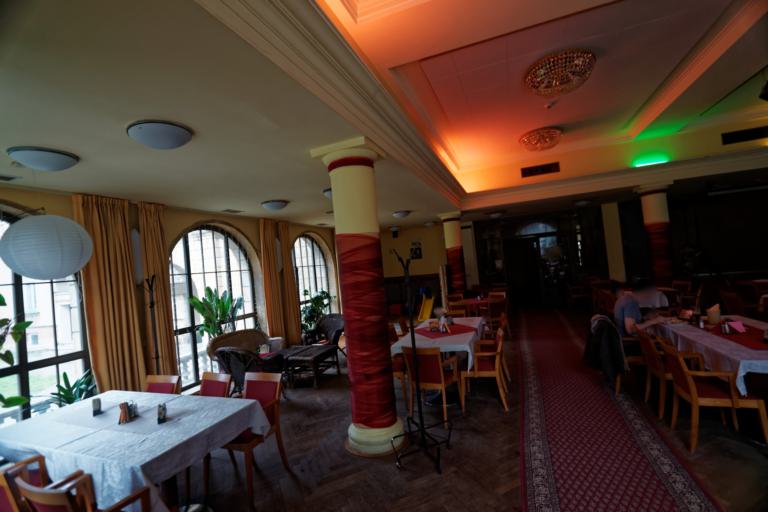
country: CZ
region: Moravskoslezsky
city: Havirov
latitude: 49.7819
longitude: 18.4256
